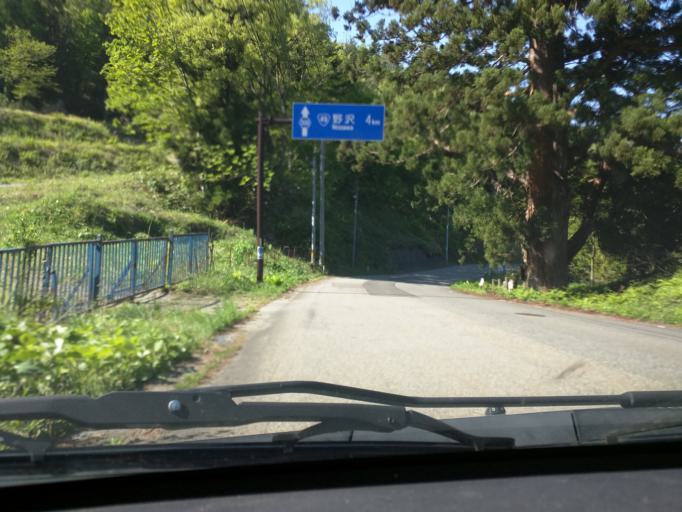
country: JP
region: Fukushima
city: Kitakata
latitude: 37.5606
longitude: 139.6269
